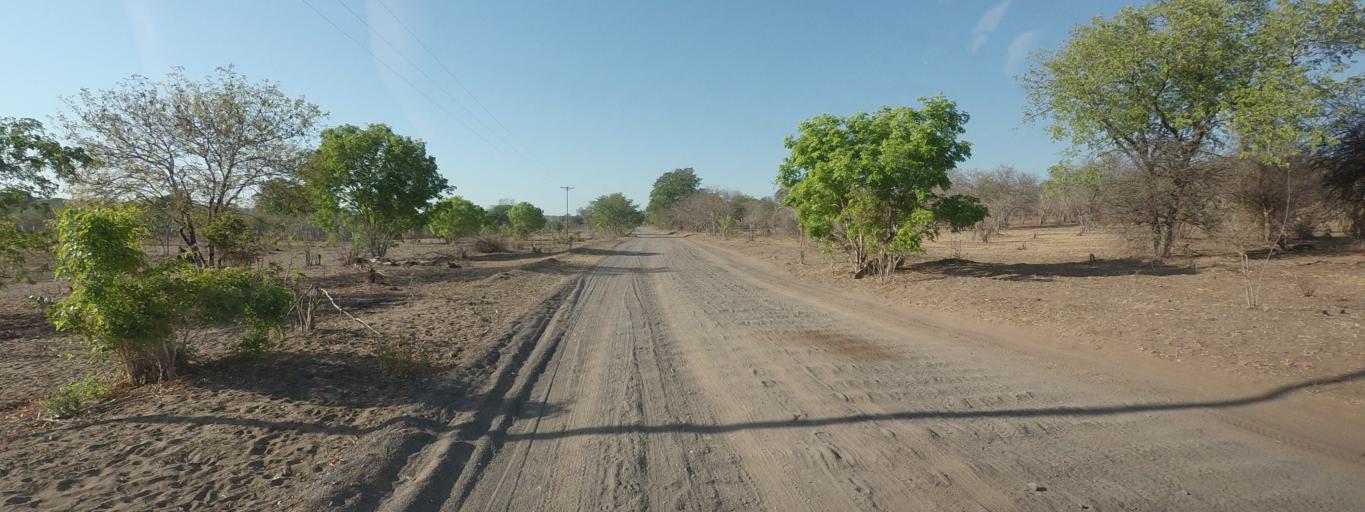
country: BW
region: North West
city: Kasane
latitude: -17.8904
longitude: 25.2294
